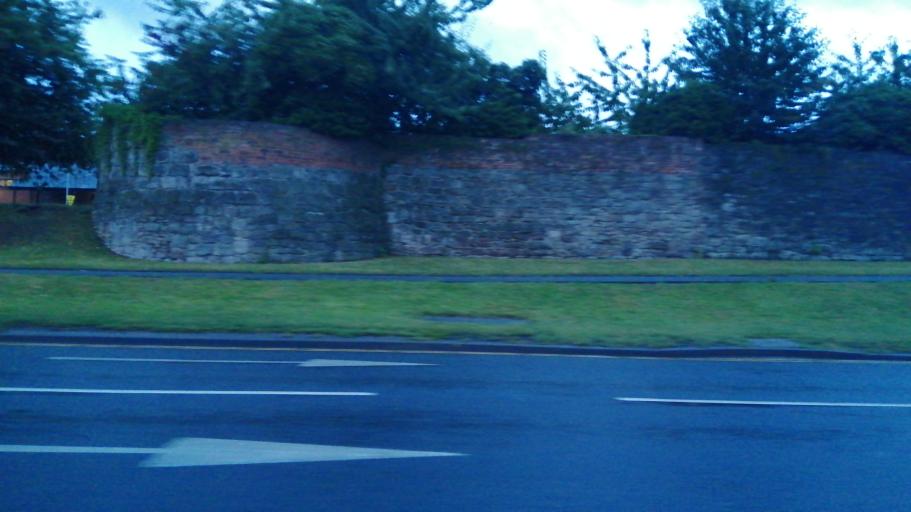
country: GB
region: England
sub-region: Herefordshire
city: Hereford
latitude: 52.0553
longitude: -2.7205
